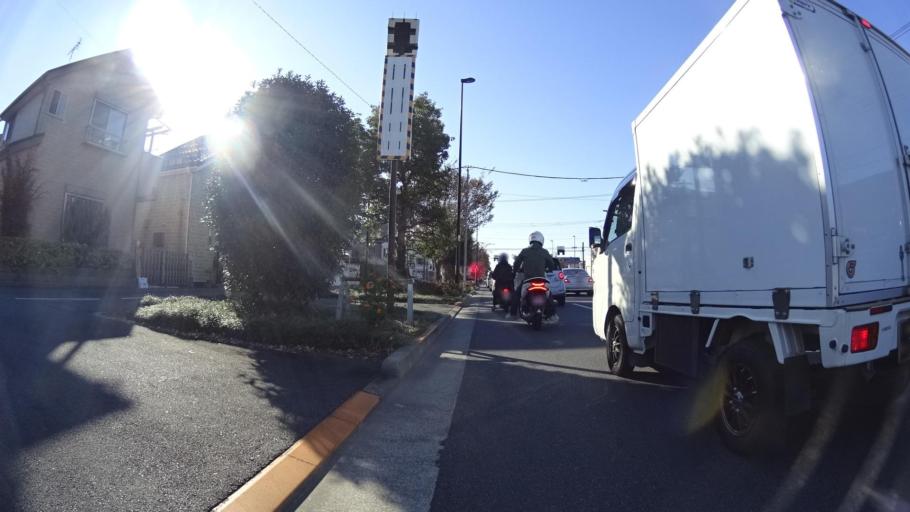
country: JP
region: Tokyo
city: Kamirenjaku
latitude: 35.6959
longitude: 139.5506
